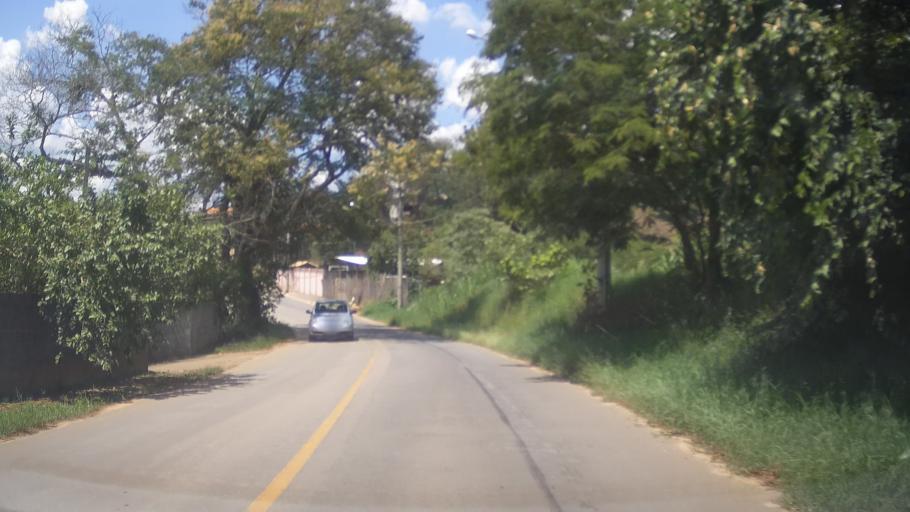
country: BR
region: Sao Paulo
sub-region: Jarinu
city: Jarinu
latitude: -23.1251
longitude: -46.8063
